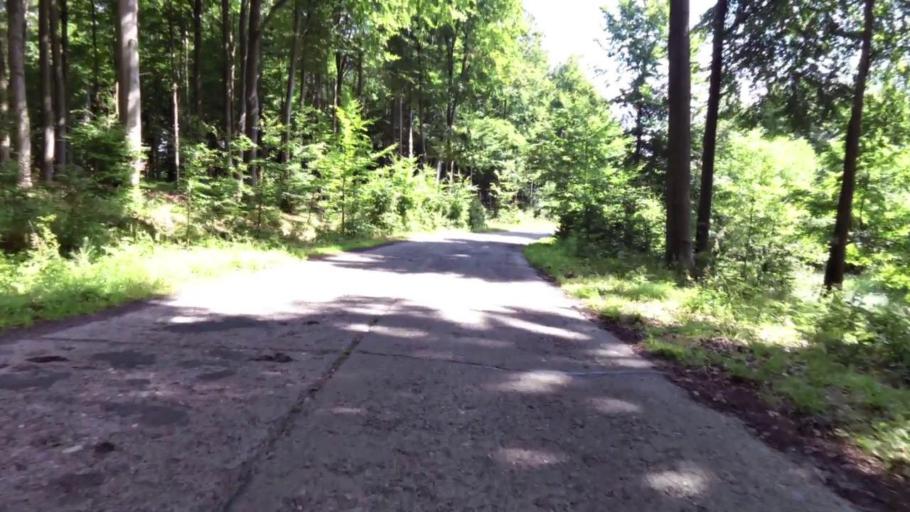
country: PL
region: West Pomeranian Voivodeship
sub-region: Powiat stargardzki
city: Insko
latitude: 53.4038
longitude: 15.5214
